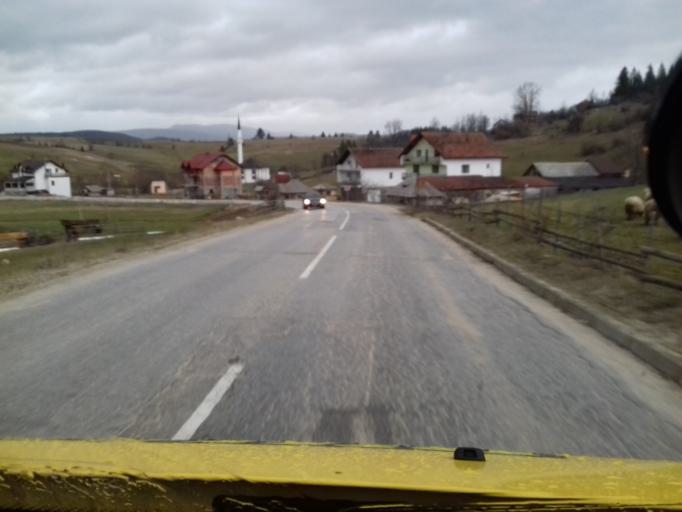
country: BA
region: Federation of Bosnia and Herzegovina
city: Turbe
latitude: 44.3146
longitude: 17.5289
